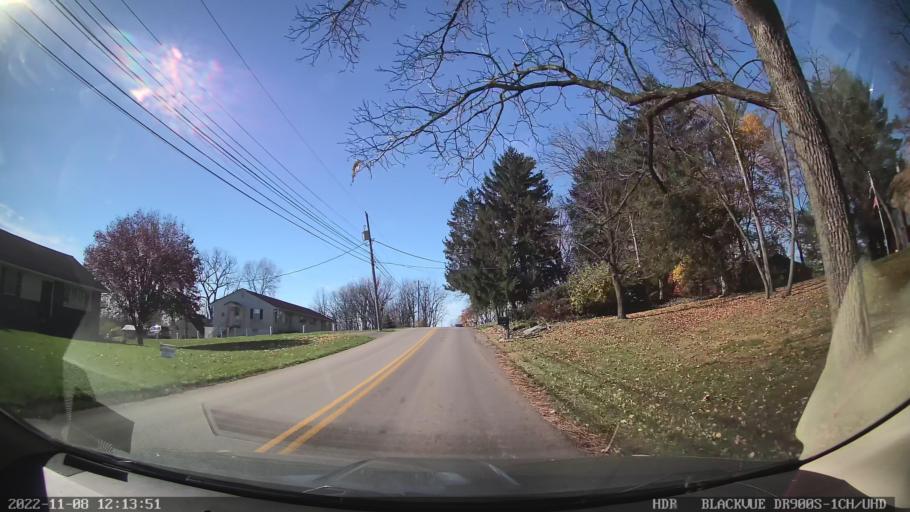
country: US
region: Pennsylvania
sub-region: Berks County
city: Kutztown
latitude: 40.5197
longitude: -75.7613
